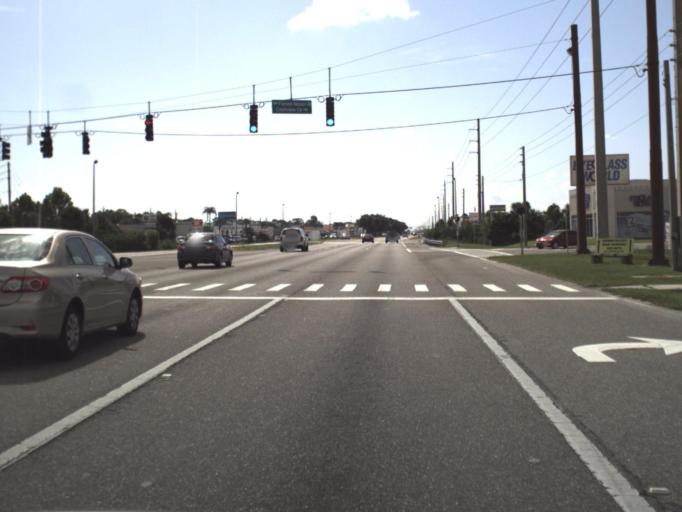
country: US
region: Florida
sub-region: Charlotte County
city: Port Charlotte
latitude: 27.0000
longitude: -82.1237
